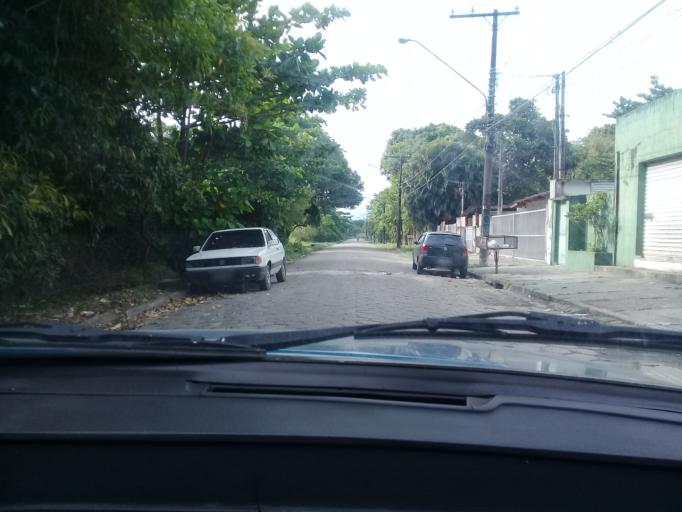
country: BR
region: Sao Paulo
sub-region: Guaruja
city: Guaruja
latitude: -23.9867
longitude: -46.2793
